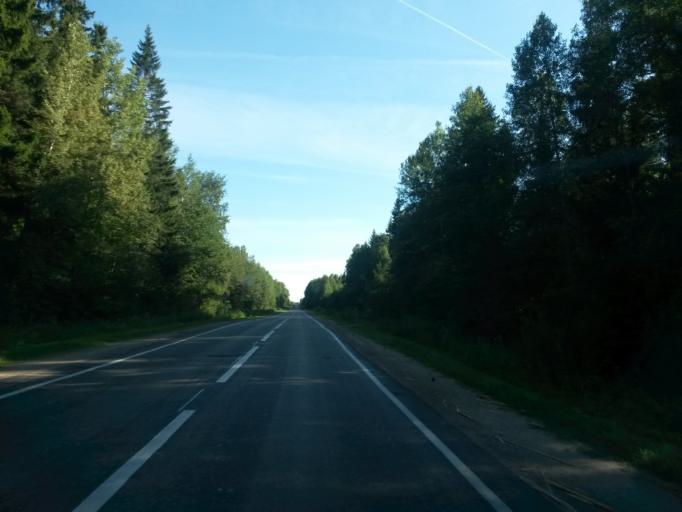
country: RU
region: Jaroslavl
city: Gavrilov-Yam
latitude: 57.4250
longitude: 39.9190
